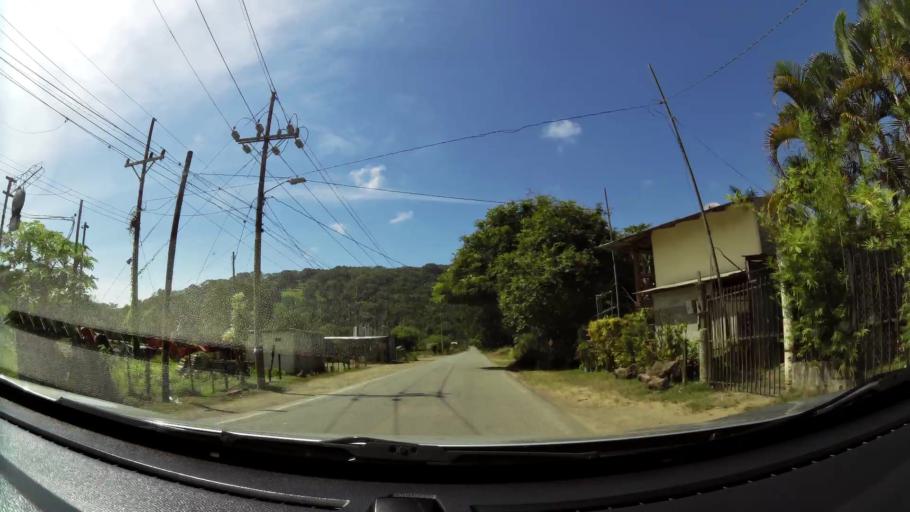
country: CR
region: San Jose
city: San Isidro
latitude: 9.2813
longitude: -83.8554
